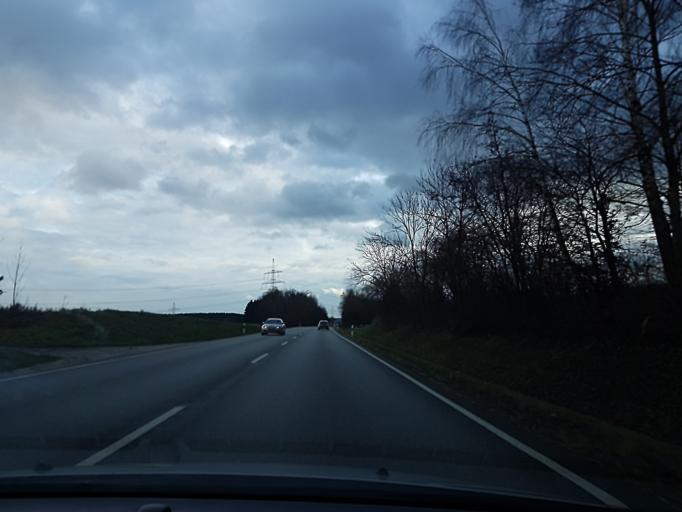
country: DE
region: Bavaria
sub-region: Lower Bavaria
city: Geisenhausen
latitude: 48.4960
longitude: 12.2255
